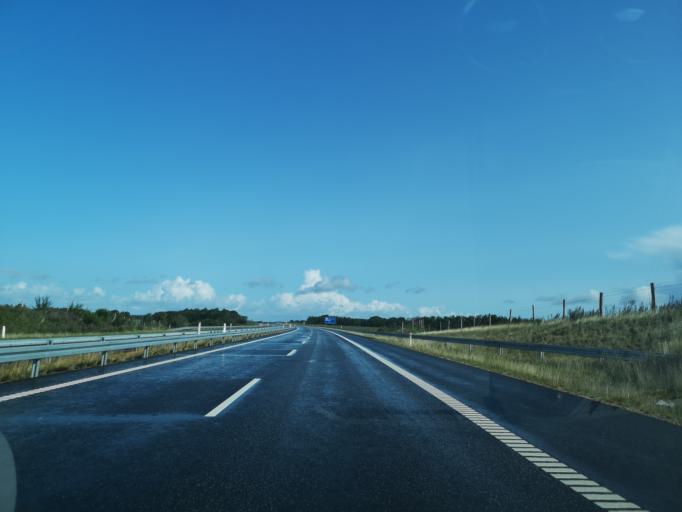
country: DK
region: Central Jutland
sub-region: Herning Kommune
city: Snejbjerg
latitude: 56.1752
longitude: 8.8924
